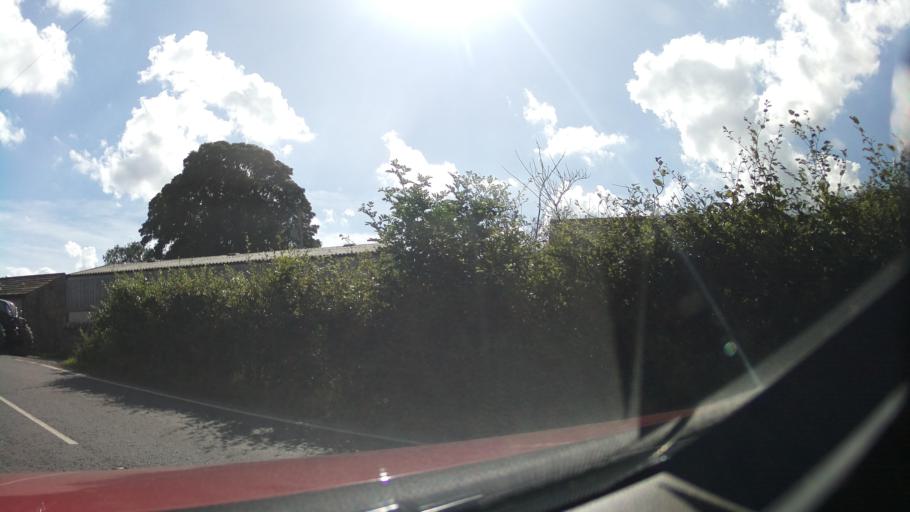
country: GB
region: England
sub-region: North Yorkshire
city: Leyburn
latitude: 54.2934
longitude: -1.8184
